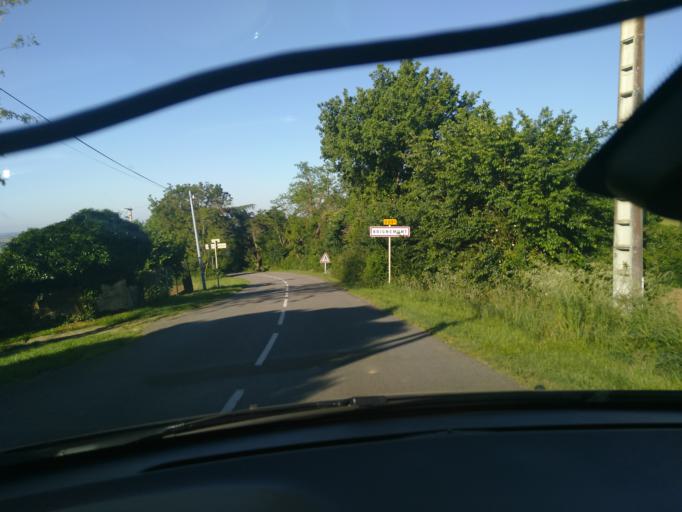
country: FR
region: Midi-Pyrenees
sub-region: Departement du Tarn-et-Garonne
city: Beaumont-de-Lomagne
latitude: 43.7832
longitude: 0.9962
